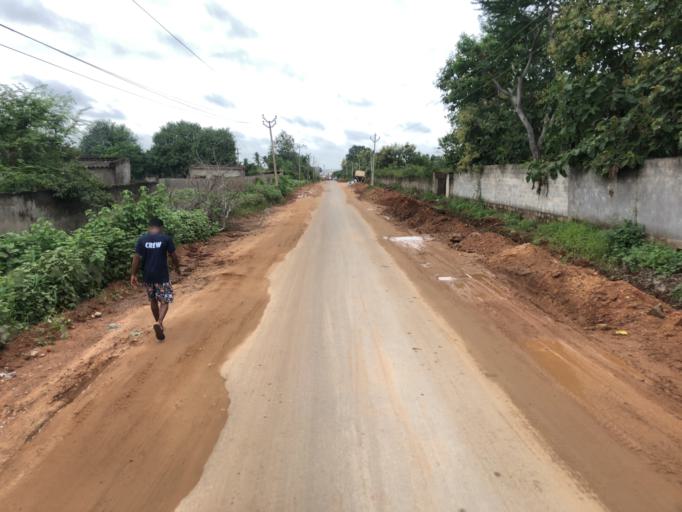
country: IN
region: Telangana
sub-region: Medak
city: Serilingampalle
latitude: 17.4269
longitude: 78.2966
